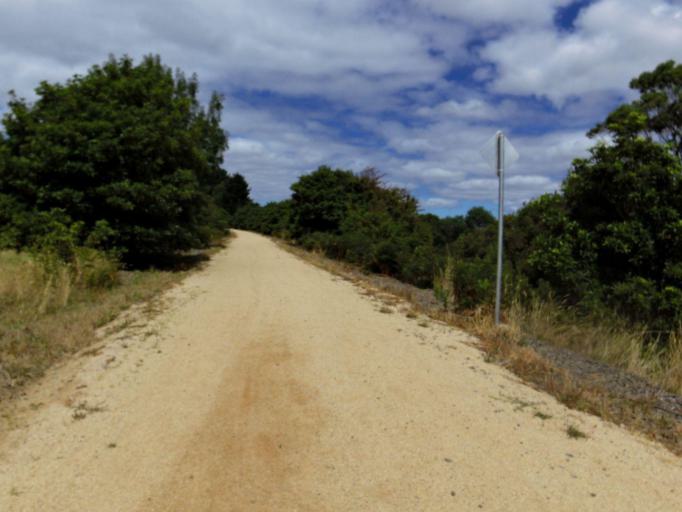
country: AU
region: Victoria
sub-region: Bass Coast
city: North Wonthaggi
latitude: -38.4157
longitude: 145.7815
